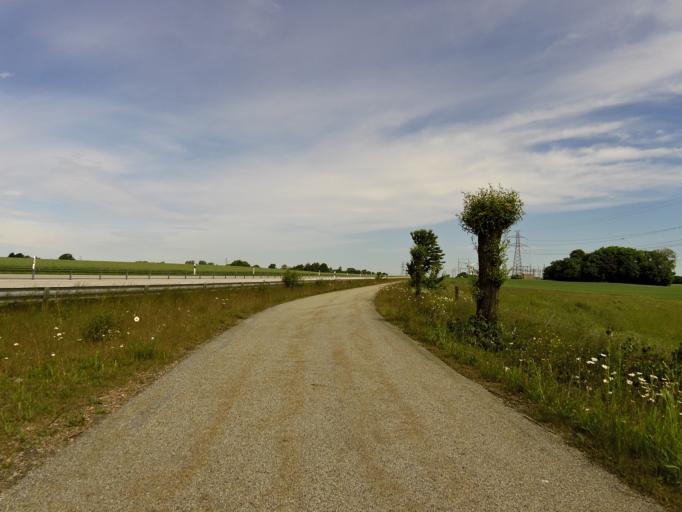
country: SE
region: Skane
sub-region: Lunds Kommun
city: Lund
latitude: 55.7355
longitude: 13.1450
